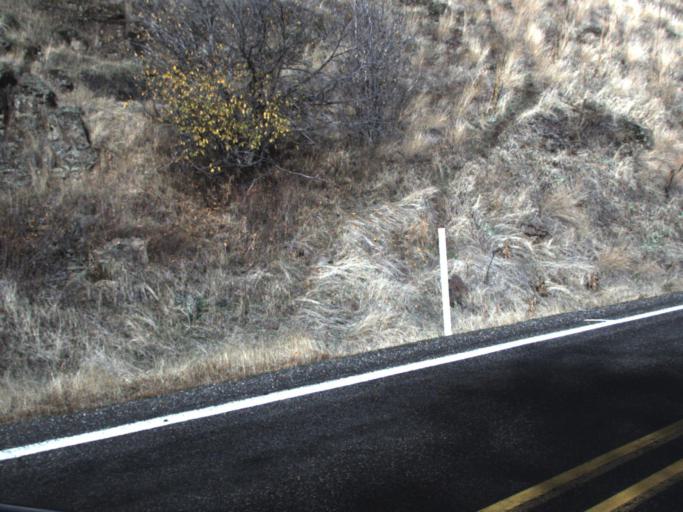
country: US
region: Washington
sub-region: Asotin County
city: Asotin
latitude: 46.0230
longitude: -117.2622
